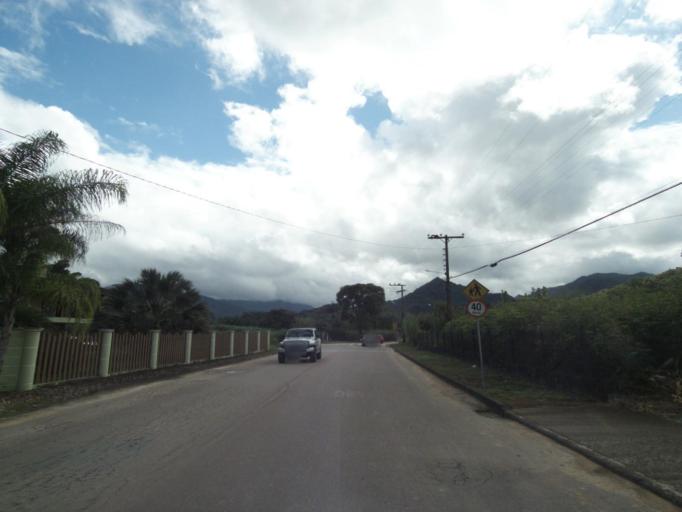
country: BR
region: Santa Catarina
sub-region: Pomerode
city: Pomerode
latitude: -26.6858
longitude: -49.1759
